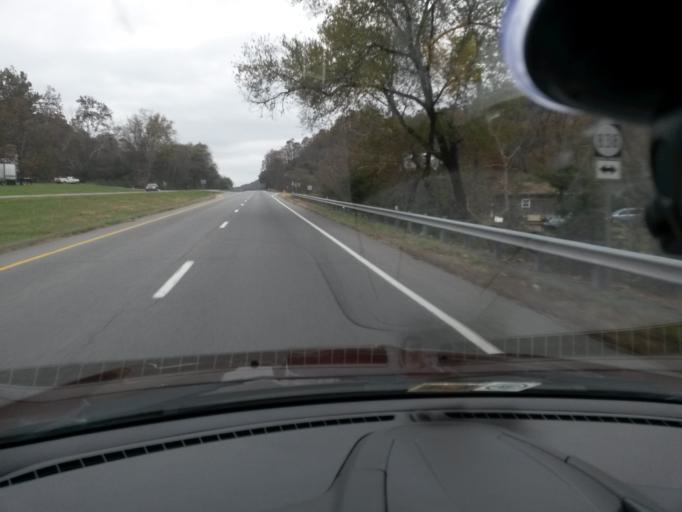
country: US
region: Virginia
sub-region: Nelson County
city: Nellysford
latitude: 37.8913
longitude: -78.7036
